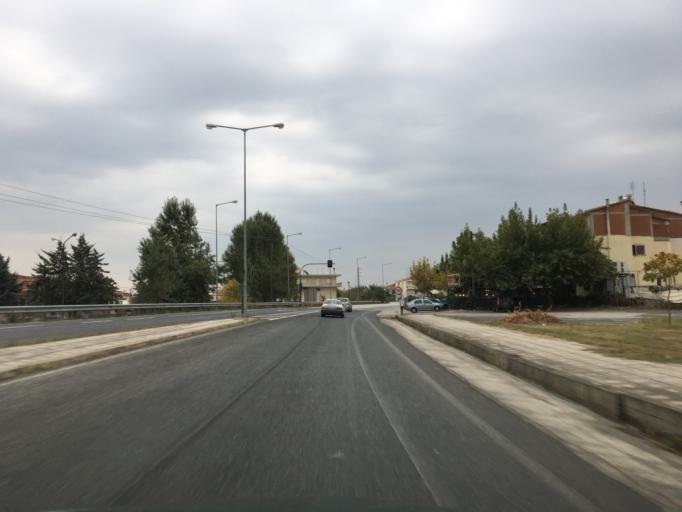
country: GR
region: Thessaly
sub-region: Trikala
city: Trikala
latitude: 39.5654
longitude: 21.7784
